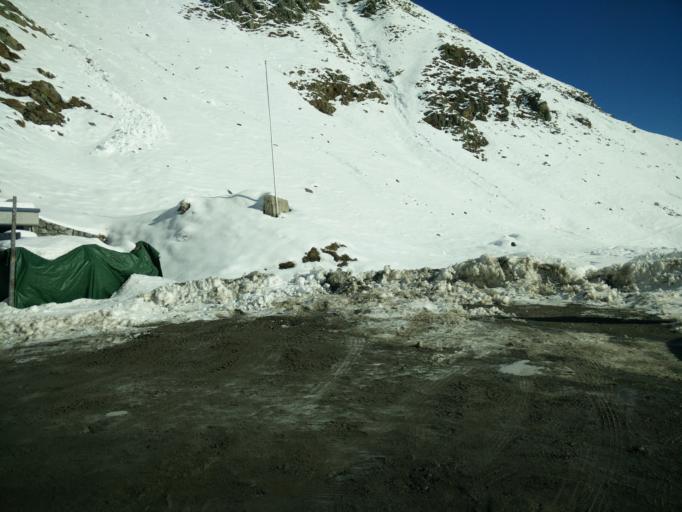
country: IT
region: Trentino-Alto Adige
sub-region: Bolzano
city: Moso in Passiria
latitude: 46.8900
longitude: 11.1117
